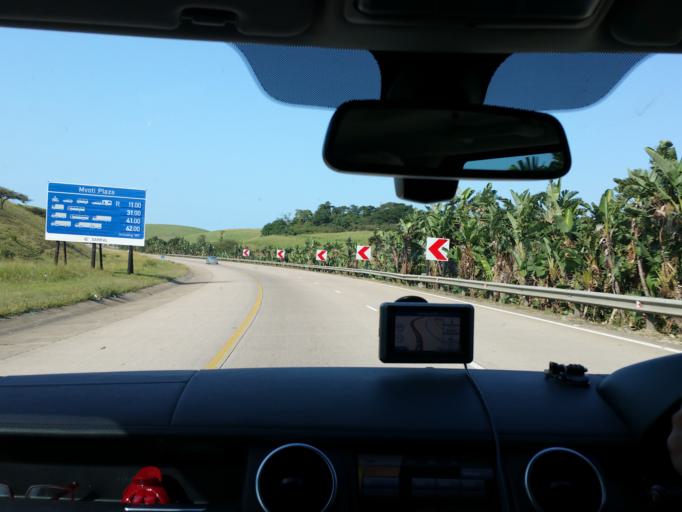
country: ZA
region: KwaZulu-Natal
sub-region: iLembe District Municipality
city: Stanger
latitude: -29.3794
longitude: 31.2955
